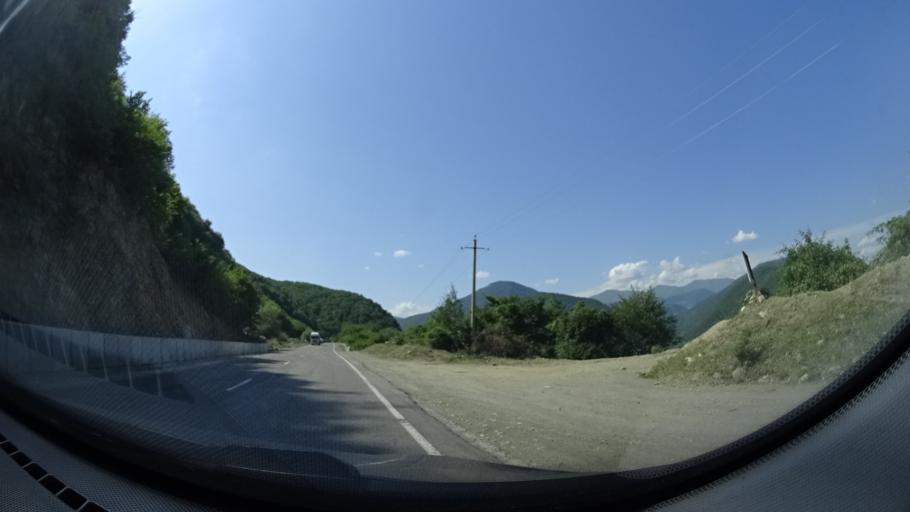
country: GE
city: Zhinvali
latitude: 42.1435
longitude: 44.7678
